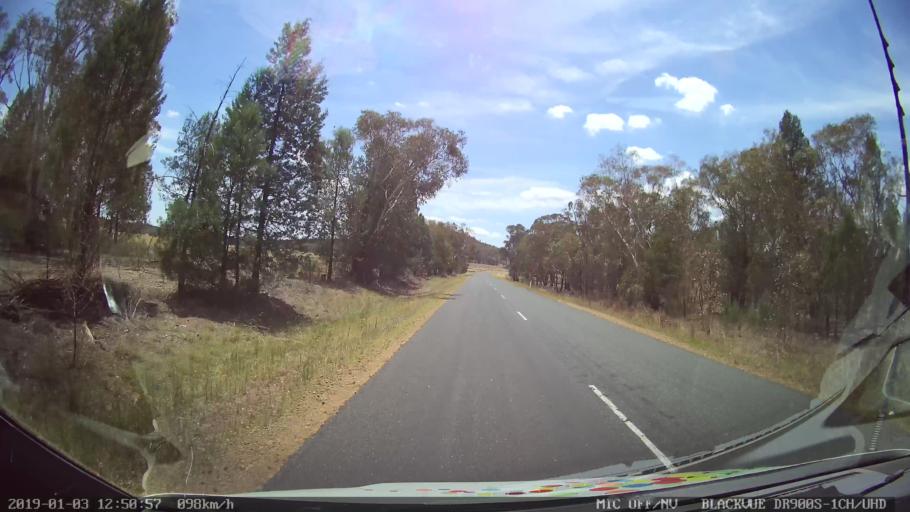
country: AU
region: New South Wales
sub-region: Weddin
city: Grenfell
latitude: -33.6852
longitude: 148.2753
